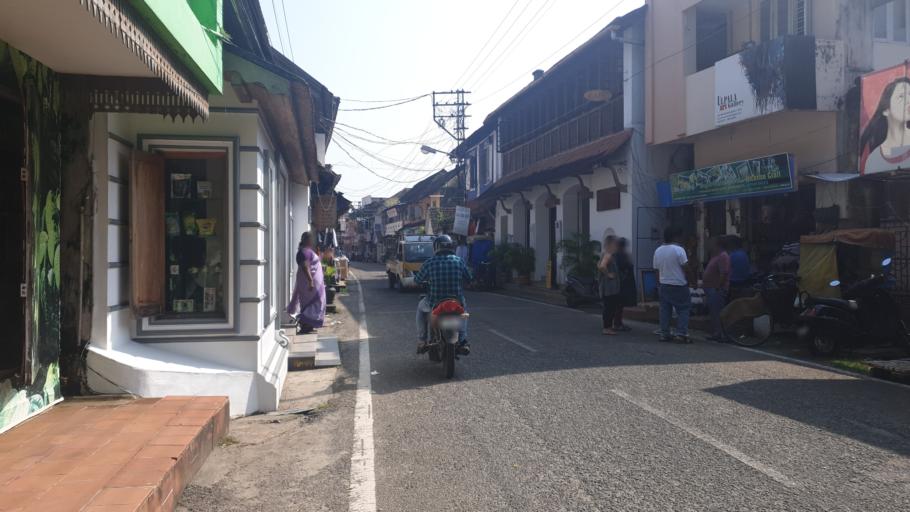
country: IN
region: Kerala
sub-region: Ernakulam
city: Cochin
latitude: 9.9577
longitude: 76.2601
